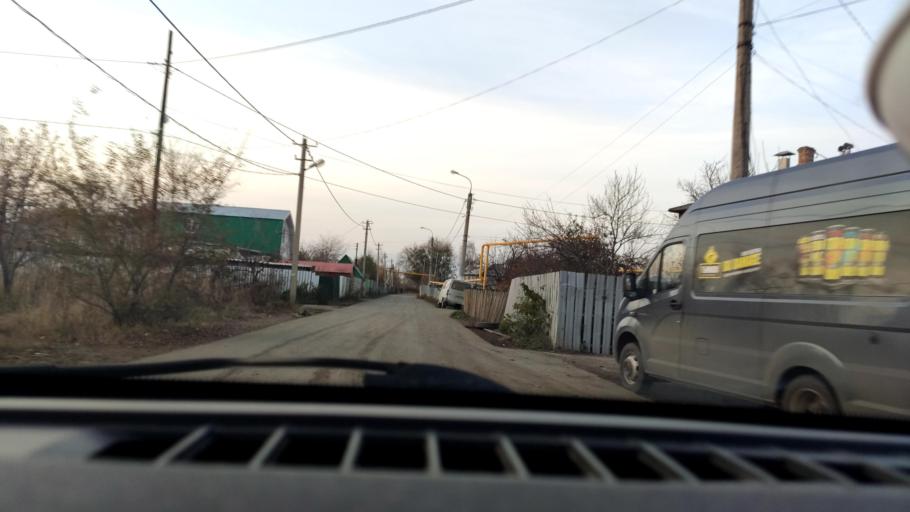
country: RU
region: Samara
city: Samara
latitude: 53.1401
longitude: 50.1346
